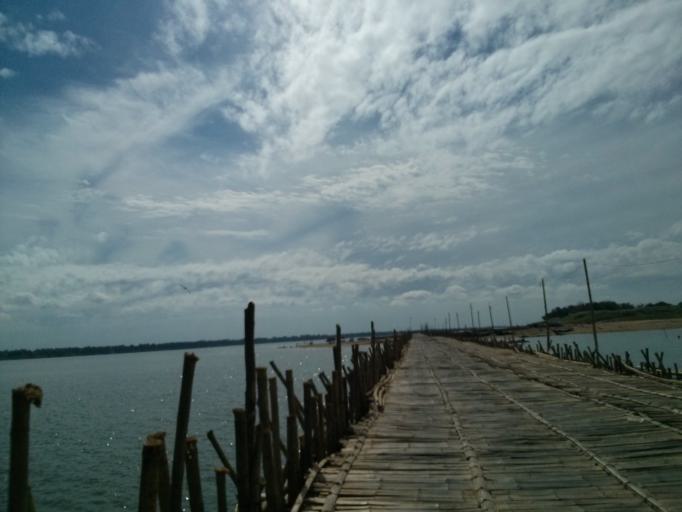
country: KH
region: Kampong Cham
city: Kampong Cham
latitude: 11.9742
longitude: 105.4623
